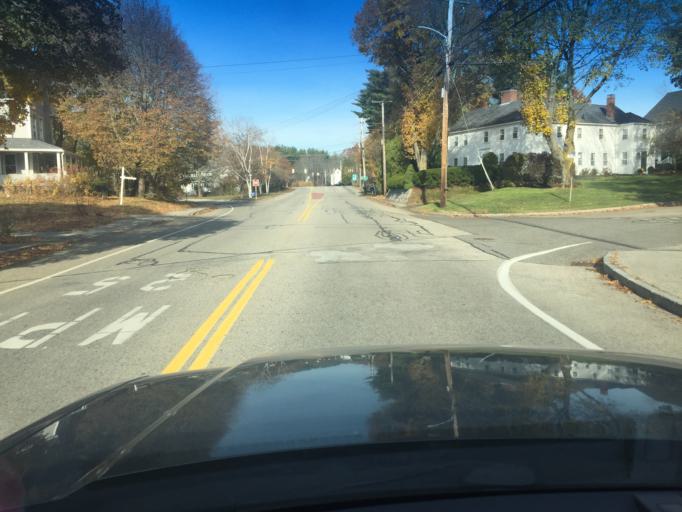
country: US
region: Maine
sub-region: York County
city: York Harbor
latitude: 43.1498
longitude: -70.6623
